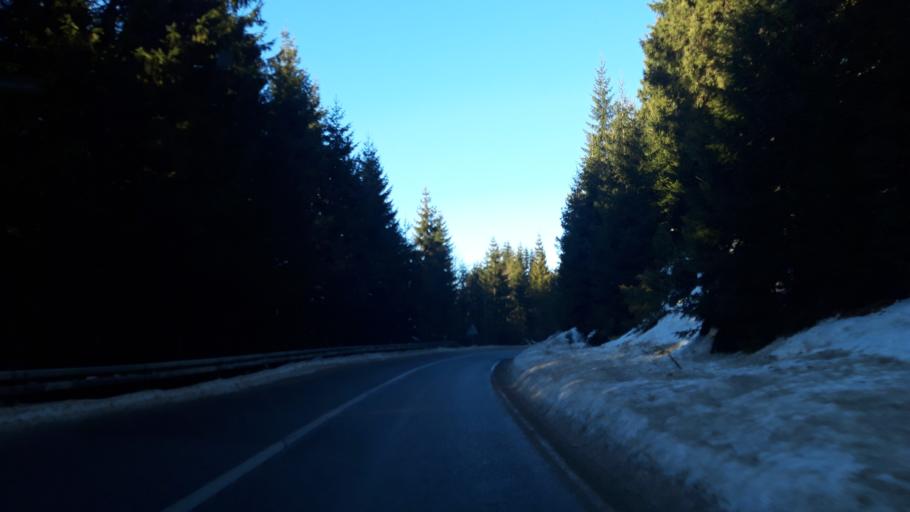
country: BA
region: Republika Srpska
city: Han Pijesak
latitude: 44.1165
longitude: 18.9699
